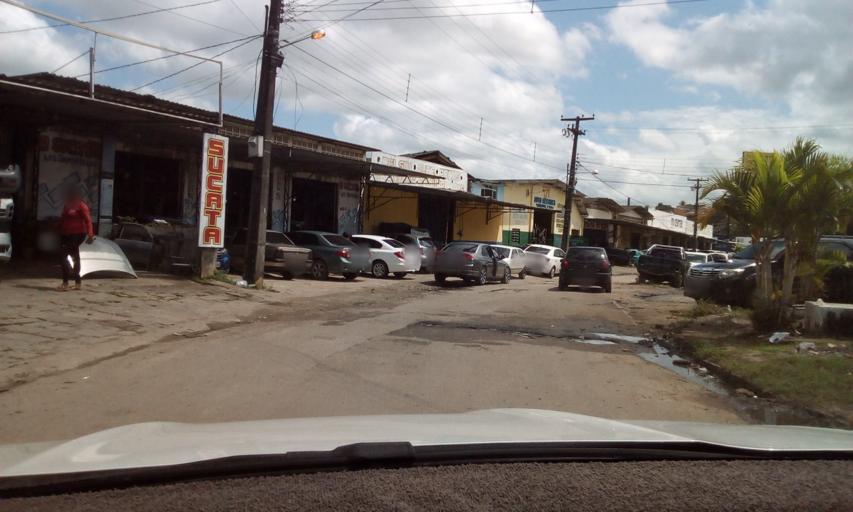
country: BR
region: Paraiba
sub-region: Joao Pessoa
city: Joao Pessoa
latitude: -7.1300
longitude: -34.8887
